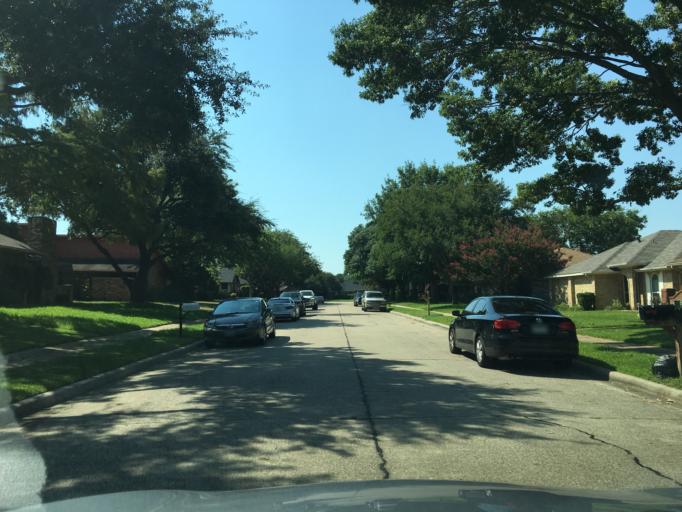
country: US
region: Texas
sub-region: Dallas County
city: Garland
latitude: 32.9364
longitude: -96.6357
